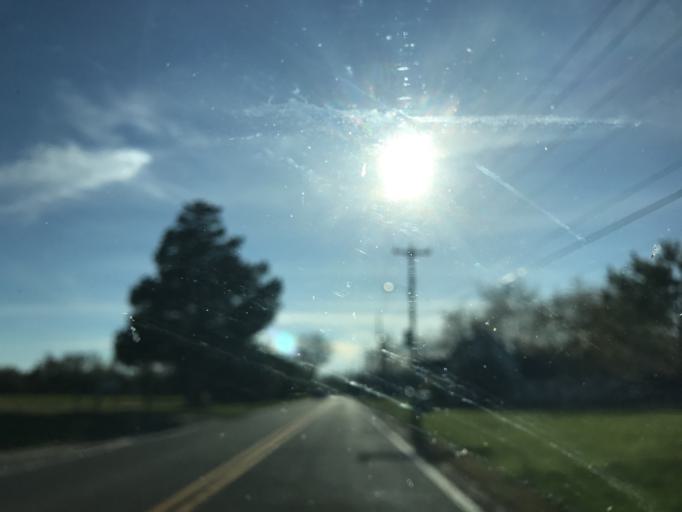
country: US
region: Maryland
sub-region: Caroline County
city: Greensboro
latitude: 39.1374
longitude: -75.7629
